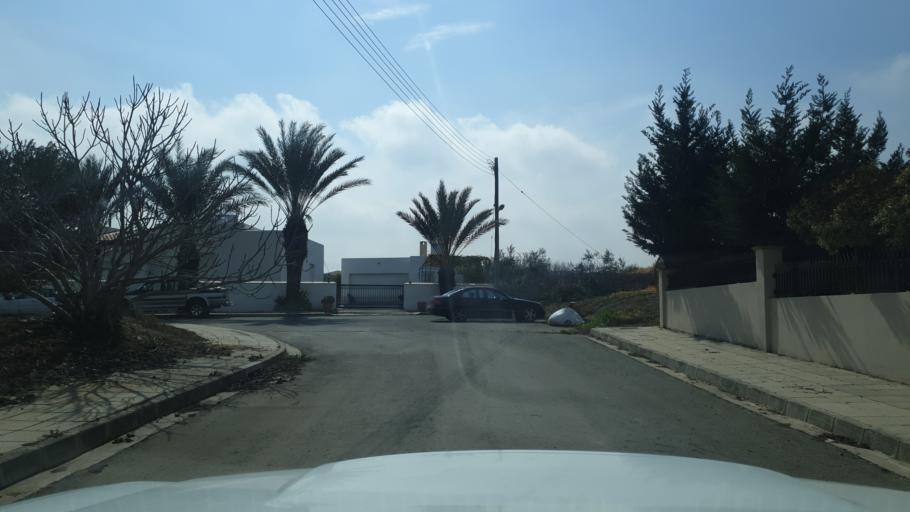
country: CY
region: Lefkosia
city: Kato Deftera
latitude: 35.0874
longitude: 33.2727
